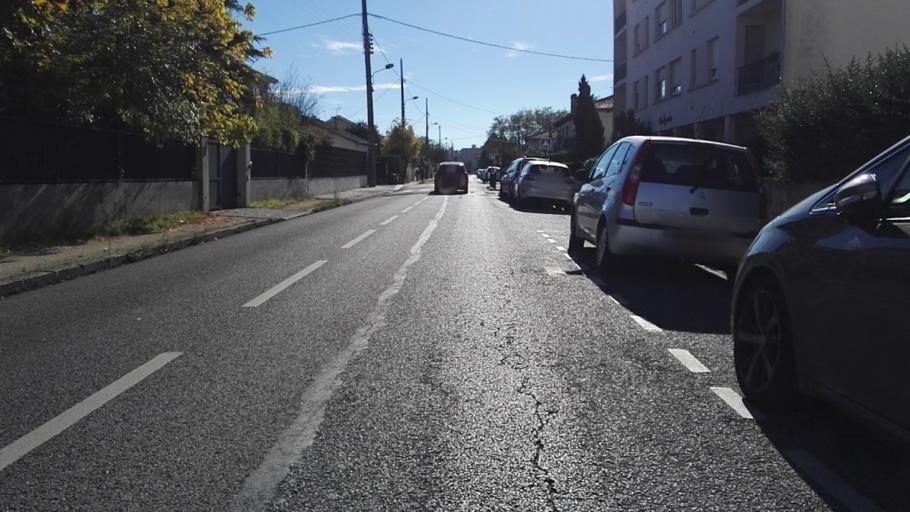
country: FR
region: Aquitaine
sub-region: Departement de la Gironde
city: Bruges
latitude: 44.8617
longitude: -0.6191
